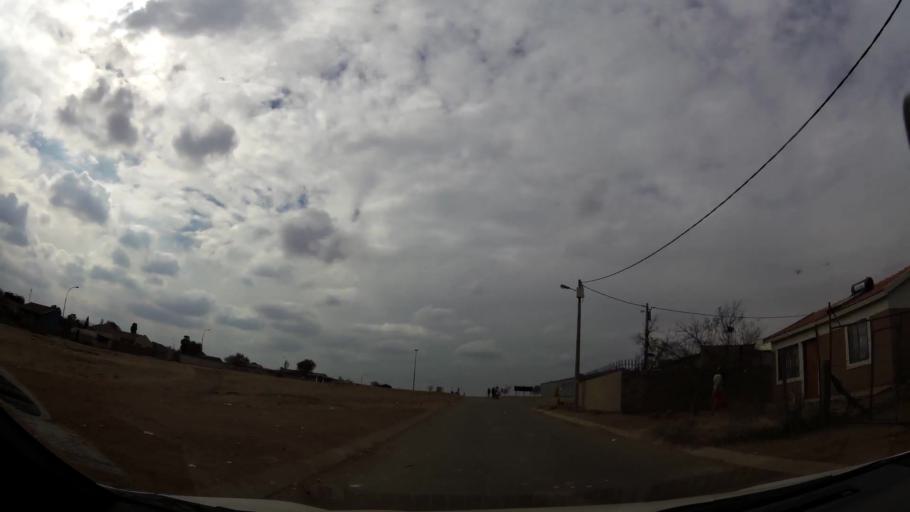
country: ZA
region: Gauteng
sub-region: Ekurhuleni Metropolitan Municipality
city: Germiston
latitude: -26.3862
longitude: 28.1323
